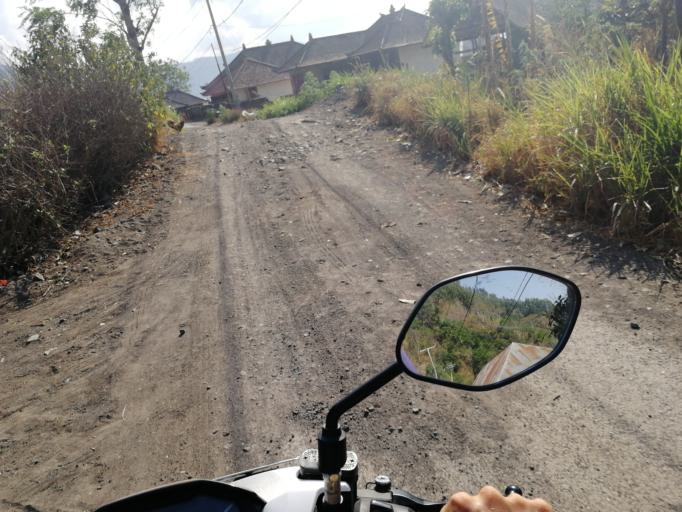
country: ID
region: Bali
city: Banjar Trunyan
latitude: -8.2638
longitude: 115.4215
